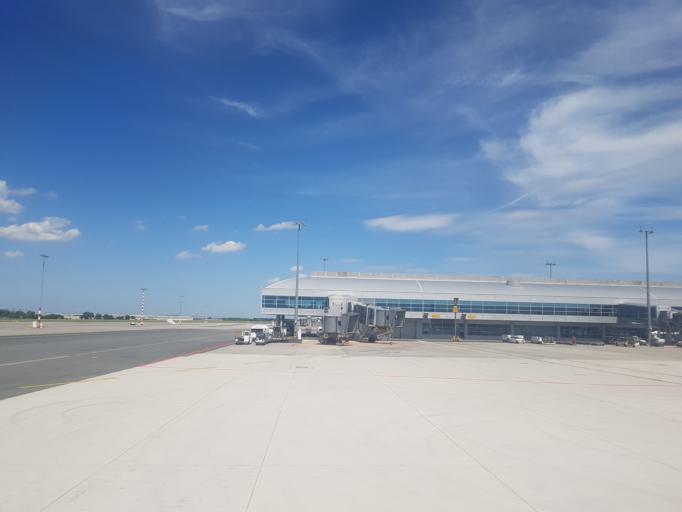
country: CZ
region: Central Bohemia
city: Hostivice
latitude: 50.1058
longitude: 14.2611
